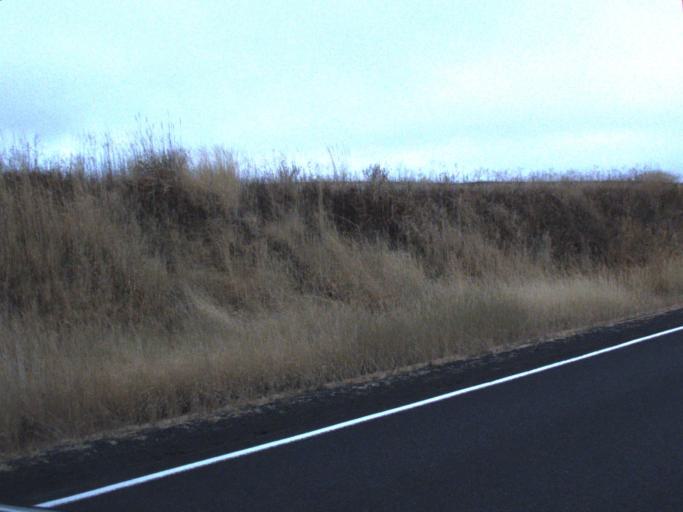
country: US
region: Washington
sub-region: Spokane County
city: Medical Lake
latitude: 47.7129
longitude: -117.8723
